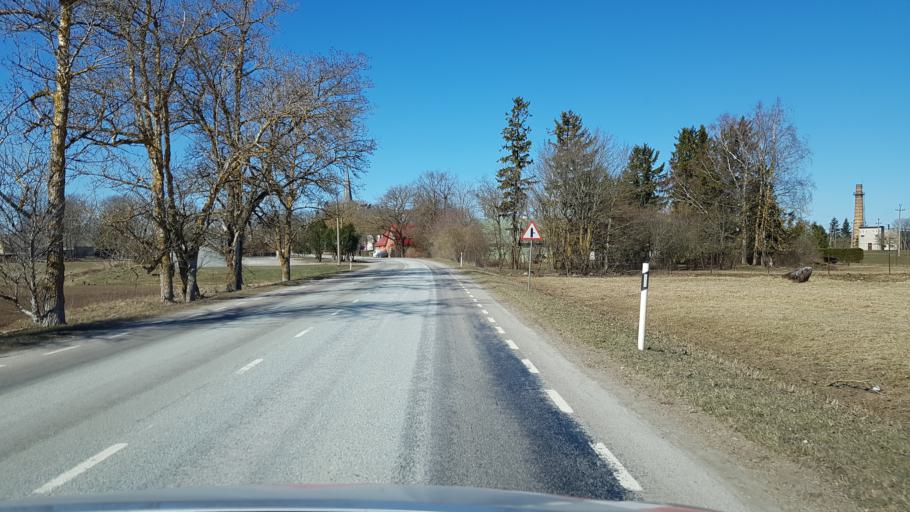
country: EE
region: Laeaene-Virumaa
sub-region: Viru-Nigula vald
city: Kunda
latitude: 59.4435
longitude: 26.6933
